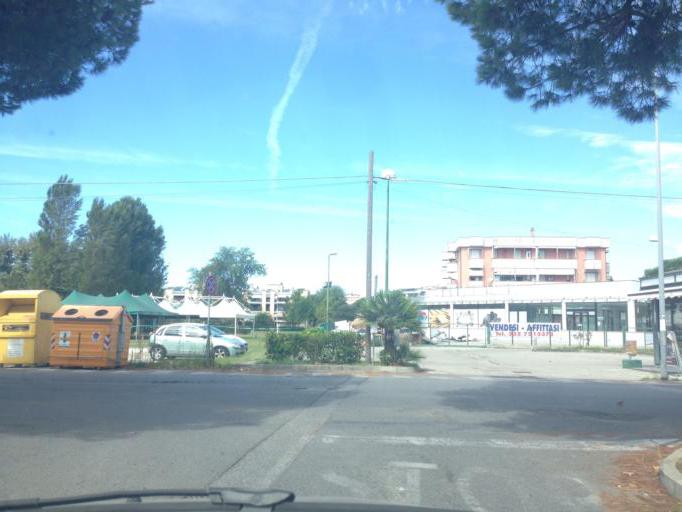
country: IT
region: Tuscany
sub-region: Provincia di Lucca
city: Camaiore
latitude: 43.8979
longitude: 10.2364
